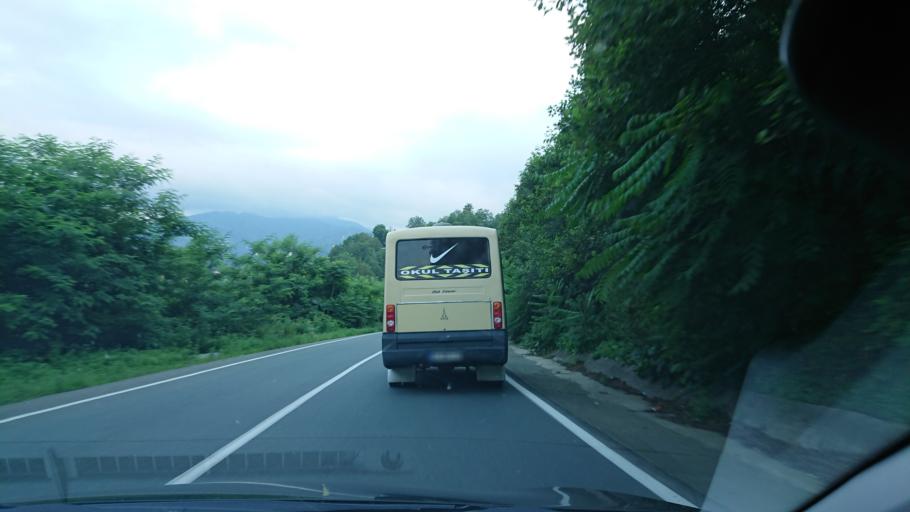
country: TR
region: Rize
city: Cayeli
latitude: 41.0712
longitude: 40.7116
